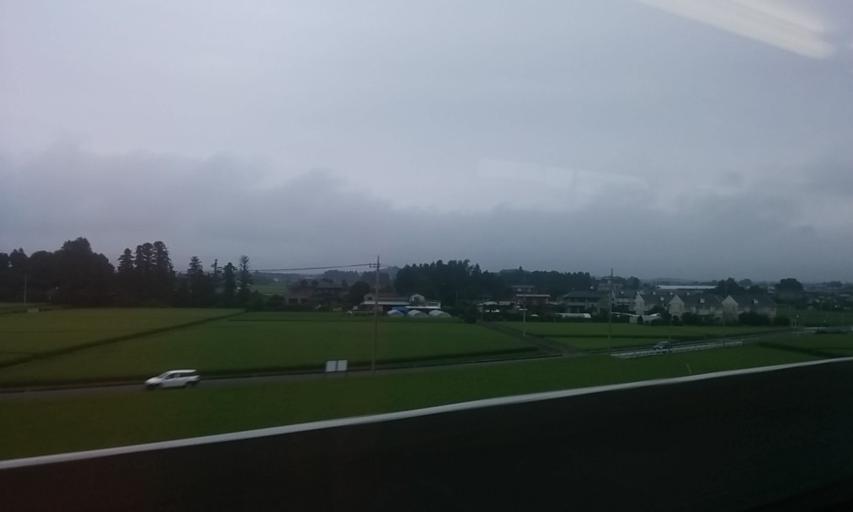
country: JP
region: Tochigi
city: Otawara
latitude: 36.8699
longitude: 139.9763
